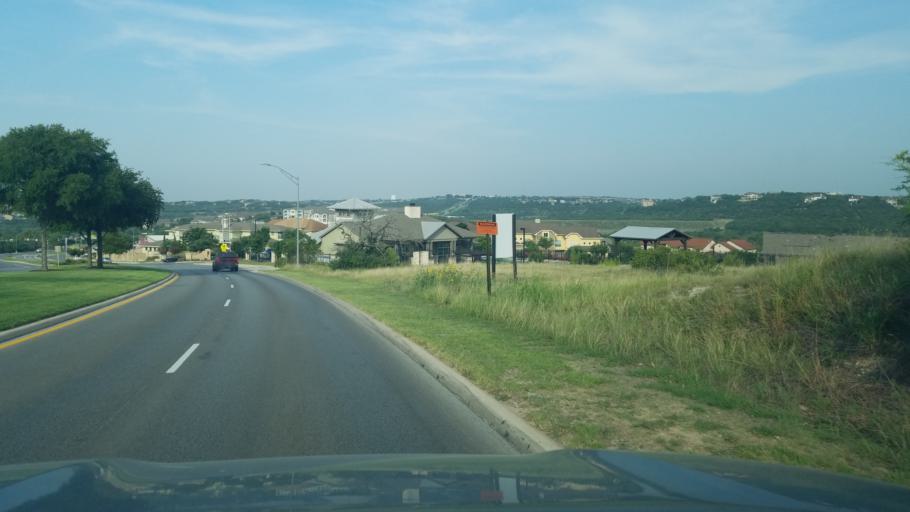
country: US
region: Texas
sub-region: Bexar County
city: Hollywood Park
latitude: 29.6488
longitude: -98.4642
